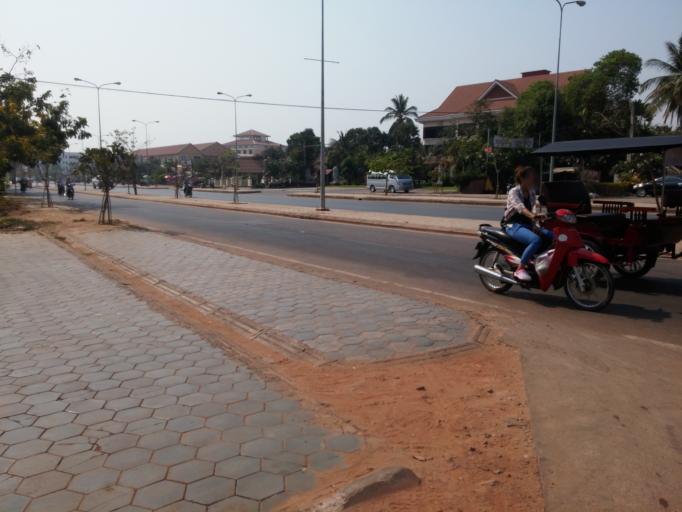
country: KH
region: Siem Reap
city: Siem Reap
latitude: 13.3689
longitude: 103.8470
